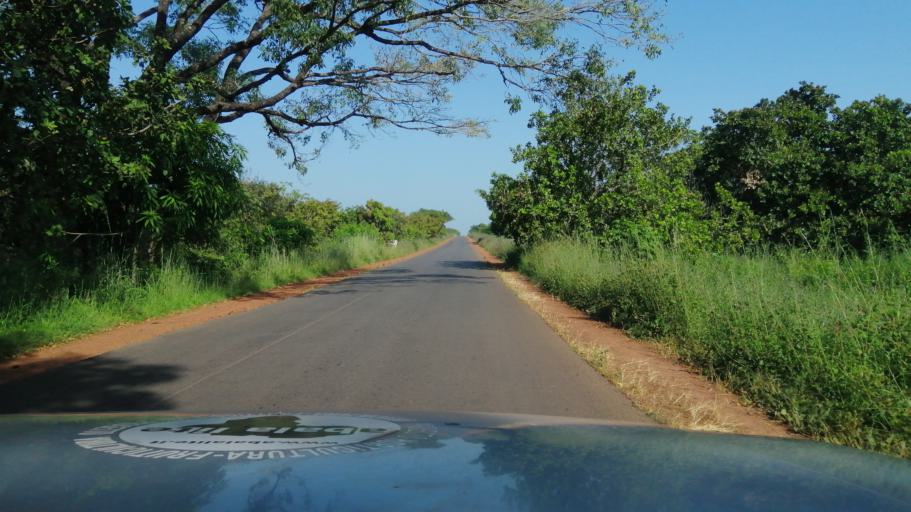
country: GW
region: Bissau
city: Bissau
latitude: 11.9588
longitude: -15.5282
